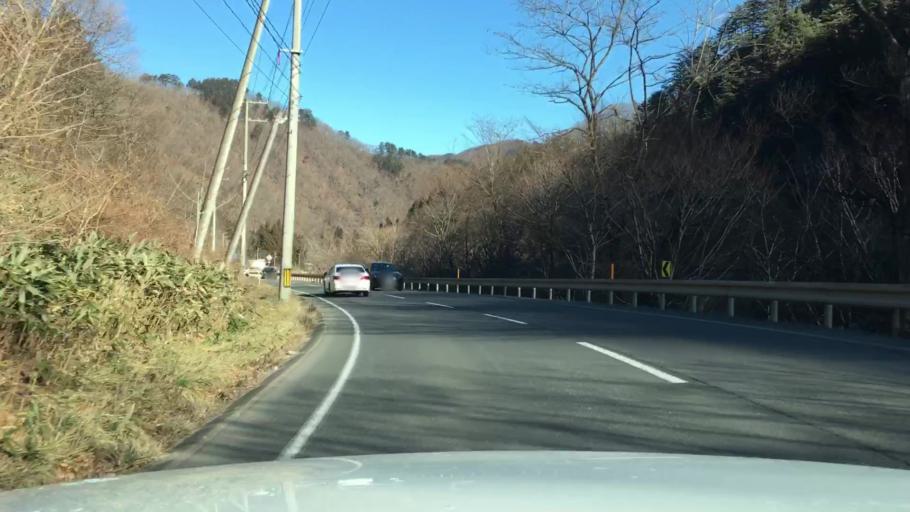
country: JP
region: Iwate
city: Miyako
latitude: 39.6099
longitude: 141.7881
